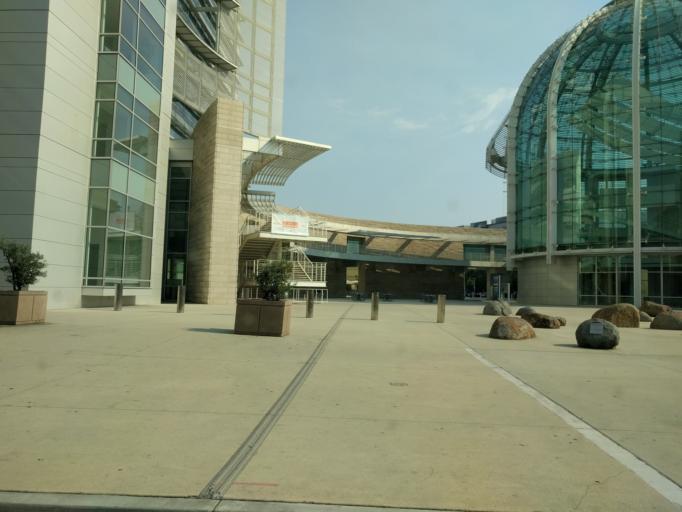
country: US
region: California
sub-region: Santa Clara County
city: San Jose
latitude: 37.3382
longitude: -121.8860
